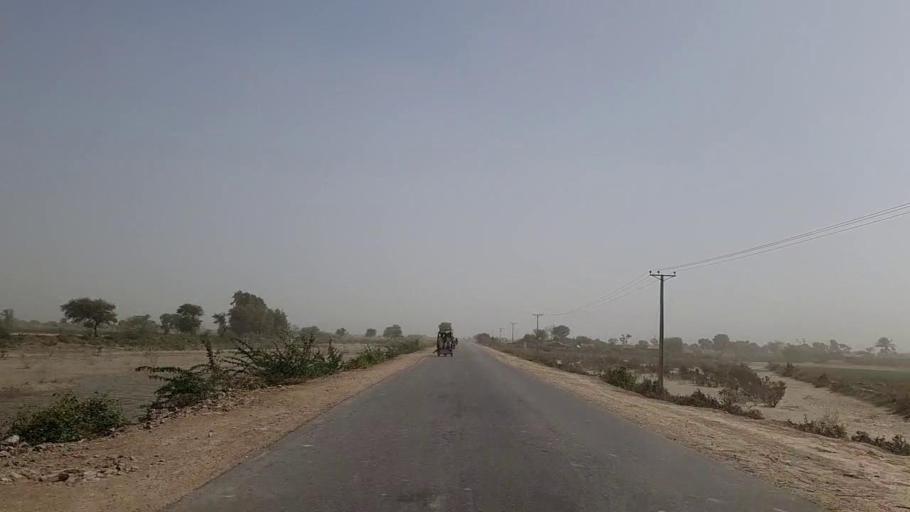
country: PK
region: Sindh
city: Talhar
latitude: 24.8710
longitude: 68.8408
